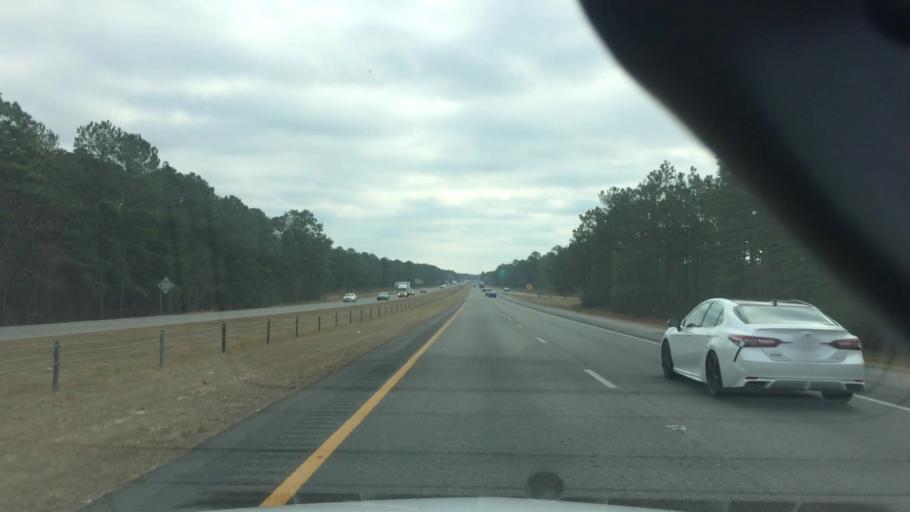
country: US
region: North Carolina
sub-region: New Hanover County
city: Castle Hayne
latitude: 34.3514
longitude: -77.8843
